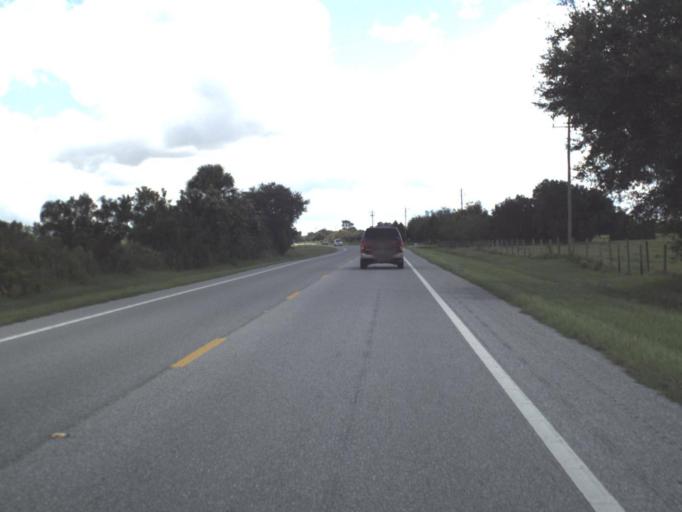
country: US
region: Florida
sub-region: DeSoto County
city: Arcadia
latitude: 27.3119
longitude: -82.1036
